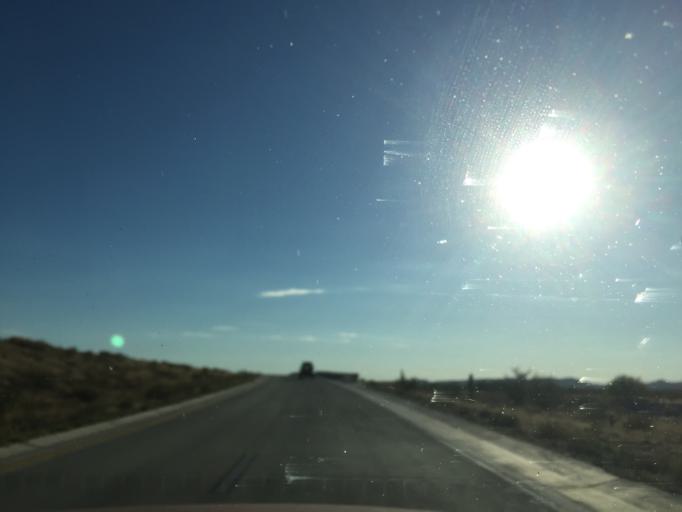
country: US
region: Arizona
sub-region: Maricopa County
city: Anthem
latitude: 33.7820
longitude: -112.2050
